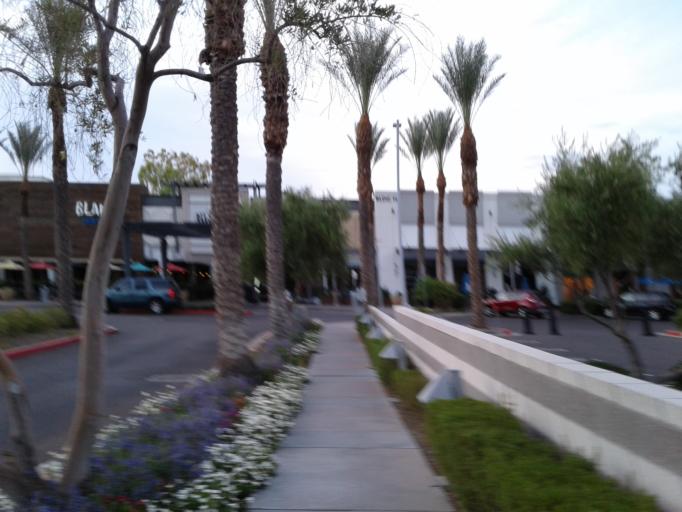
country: US
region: Arizona
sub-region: Maricopa County
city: Phoenix
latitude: 33.5099
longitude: -112.0282
